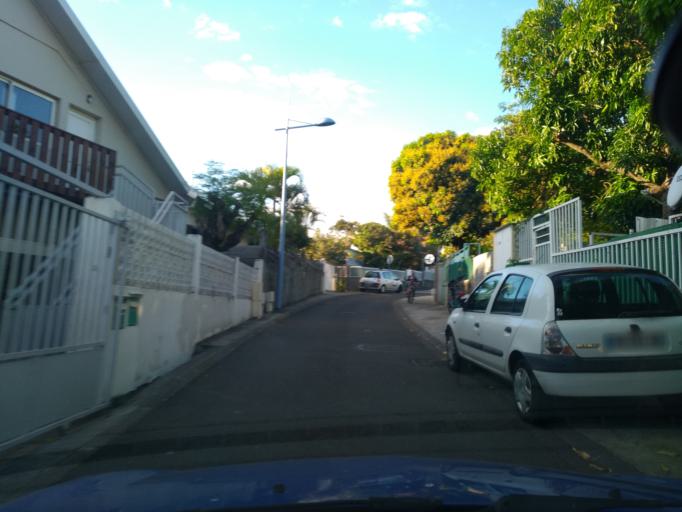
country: RE
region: Reunion
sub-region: Reunion
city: Saint-Pierre
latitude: -21.3415
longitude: 55.4805
